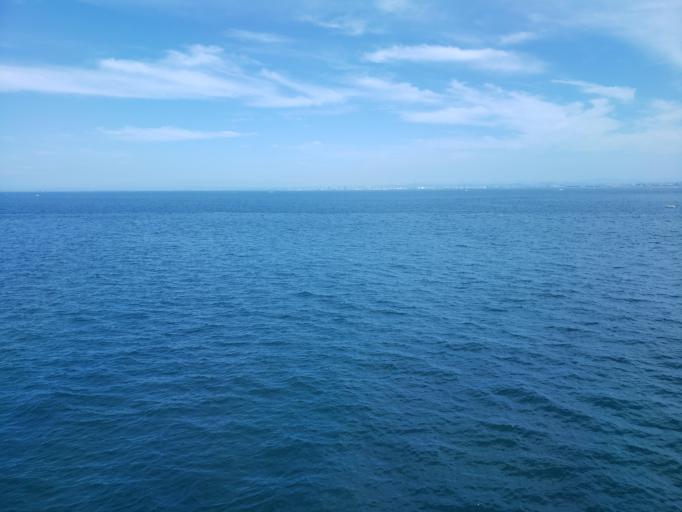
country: JP
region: Hyogo
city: Akashi
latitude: 34.6029
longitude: 134.9204
